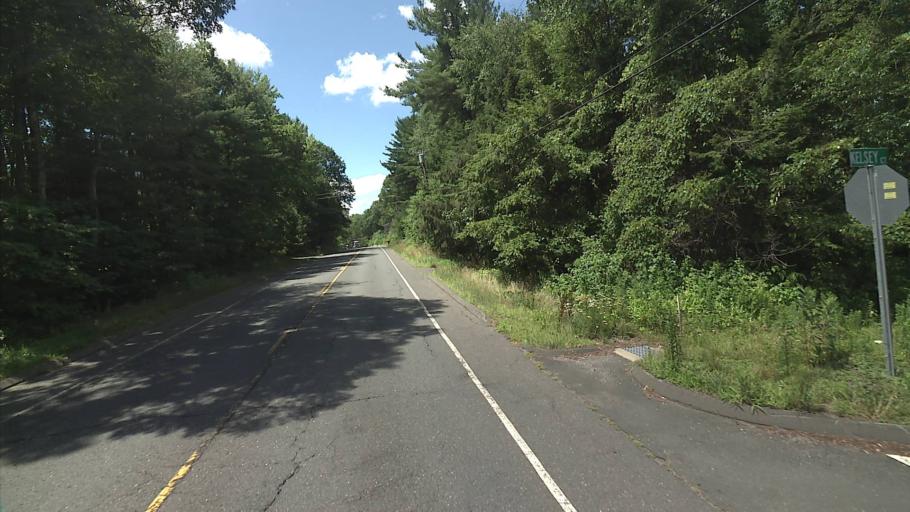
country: US
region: Connecticut
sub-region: Hartford County
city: West Simsbury
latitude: 41.9474
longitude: -72.8991
